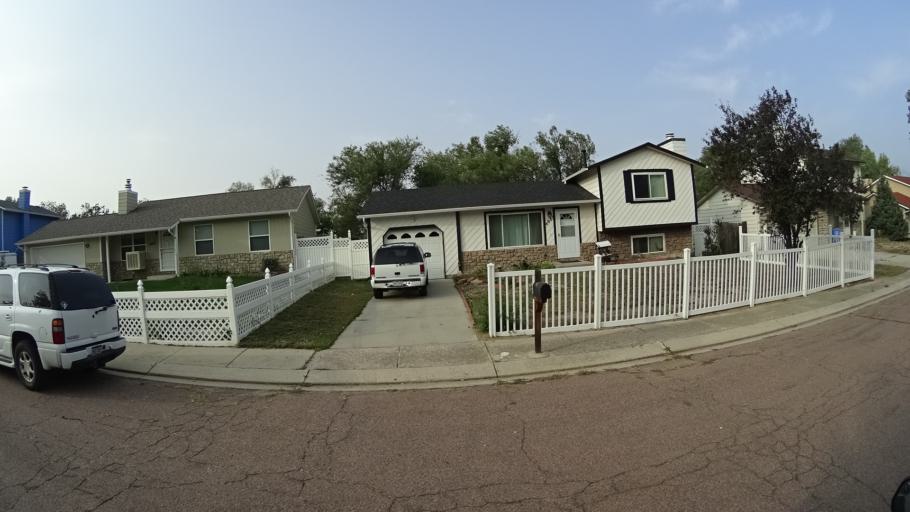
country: US
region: Colorado
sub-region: El Paso County
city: Stratmoor
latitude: 38.7996
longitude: -104.7530
